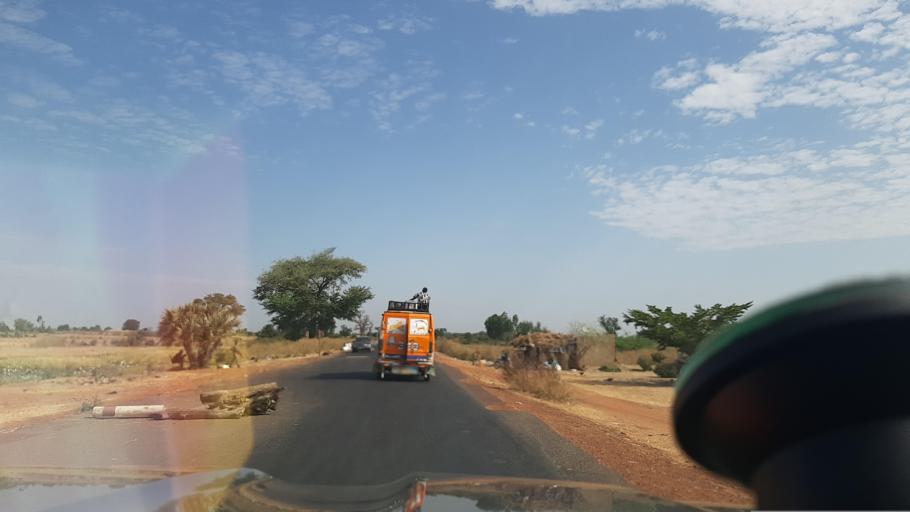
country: ML
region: Segou
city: Markala
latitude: 13.6924
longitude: -6.0997
